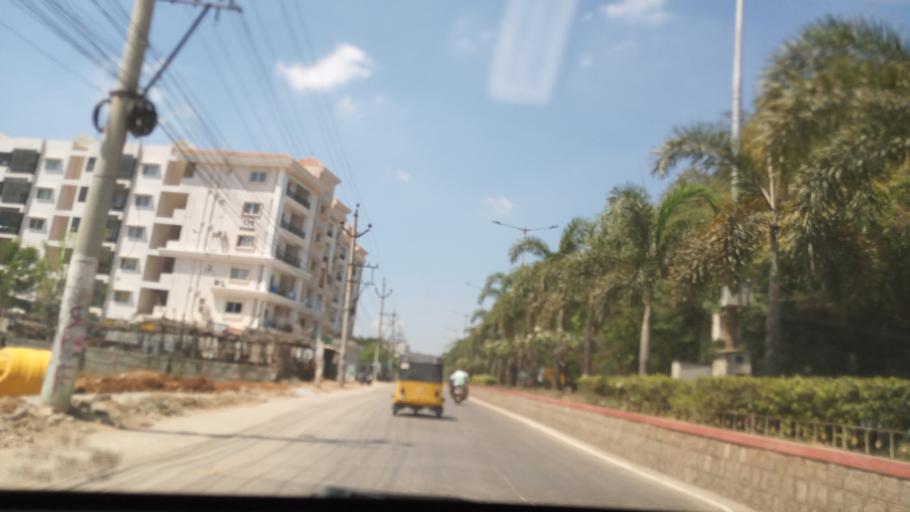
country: IN
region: Andhra Pradesh
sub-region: Chittoor
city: Akkarampalle
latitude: 13.6448
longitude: 79.4378
